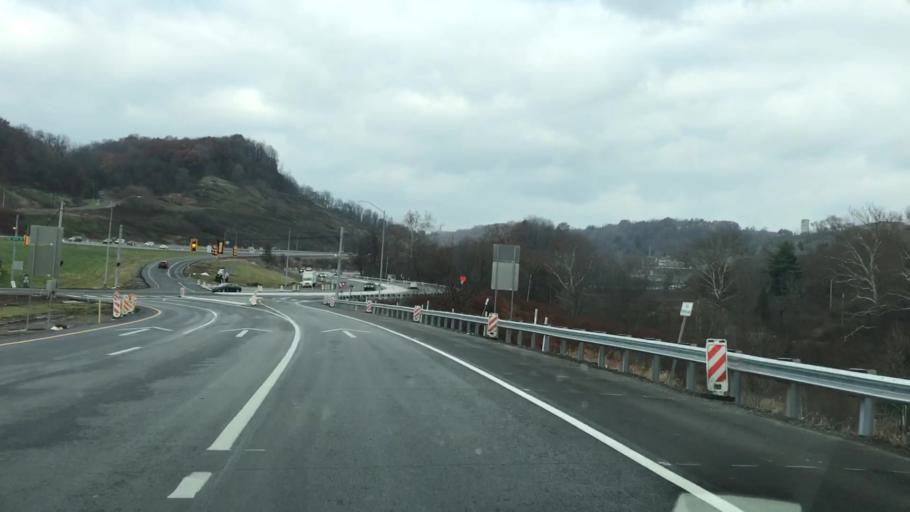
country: US
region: Pennsylvania
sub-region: Allegheny County
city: Ben Avon
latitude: 40.5248
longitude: -80.0690
